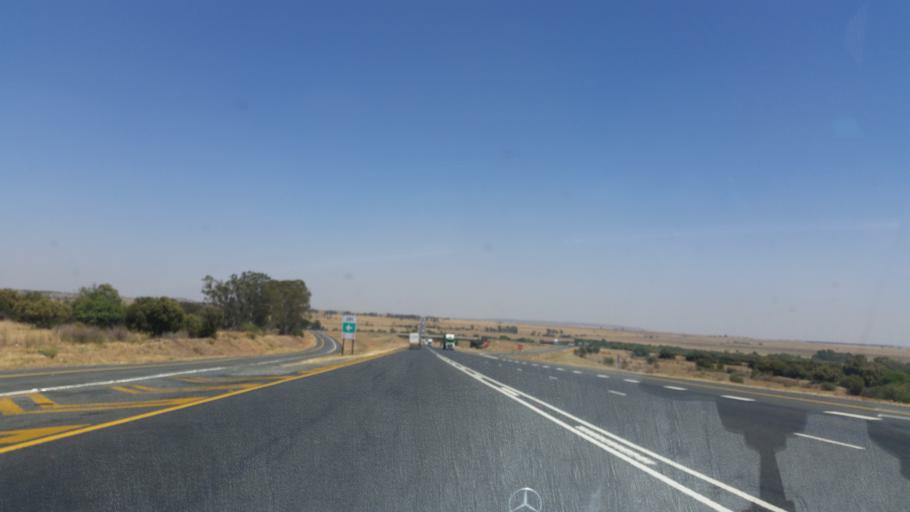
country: ZA
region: Orange Free State
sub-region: Lejweleputswa District Municipality
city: Winburg
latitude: -28.6243
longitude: 26.9144
